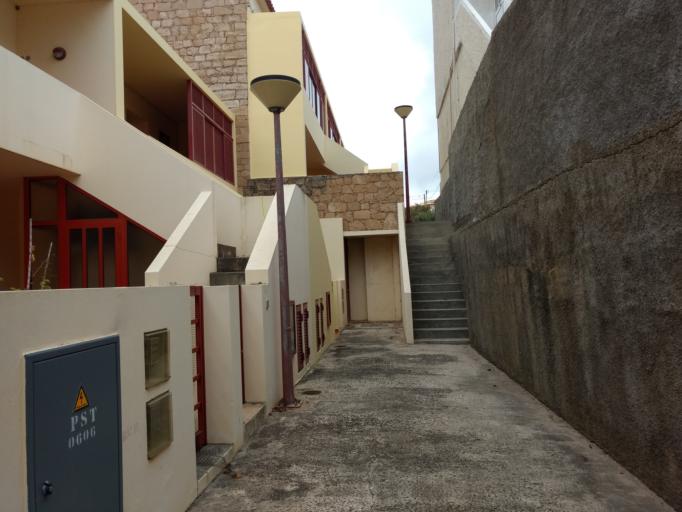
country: PT
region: Madeira
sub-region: Porto Santo
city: Vila de Porto Santo
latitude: 33.0609
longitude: -16.3310
